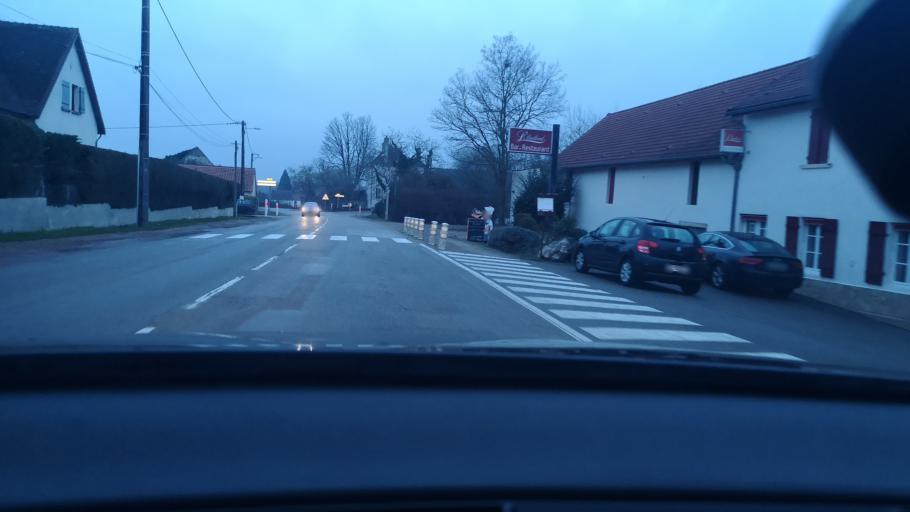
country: FR
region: Bourgogne
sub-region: Departement de Saone-et-Loire
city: Verdun-sur-le-Doubs
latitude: 47.0069
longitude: 4.9968
